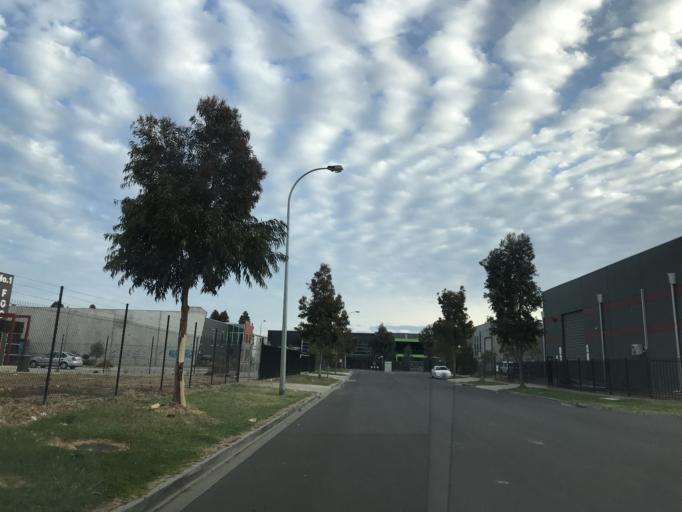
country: AU
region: Victoria
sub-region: Brimbank
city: Derrimut
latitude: -37.8034
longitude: 144.7630
